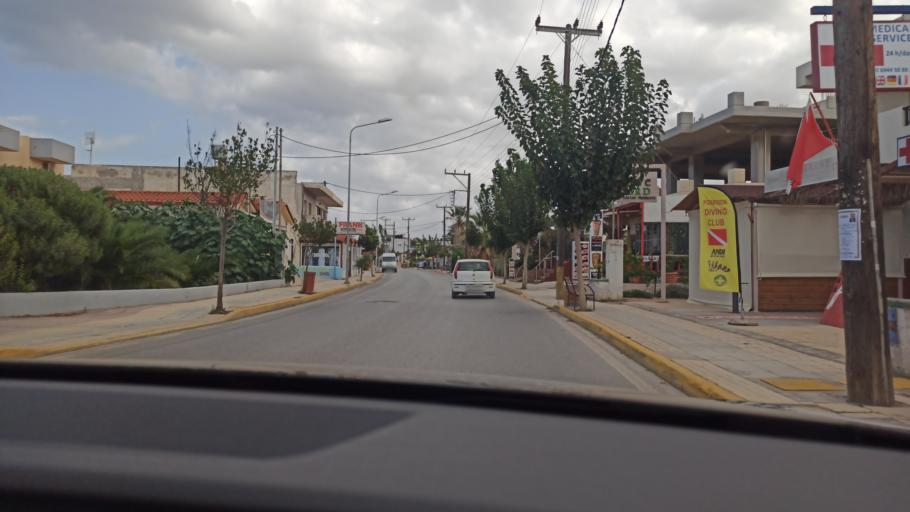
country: GR
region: Crete
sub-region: Nomos Irakleiou
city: Gazi
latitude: 35.3360
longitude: 25.0745
